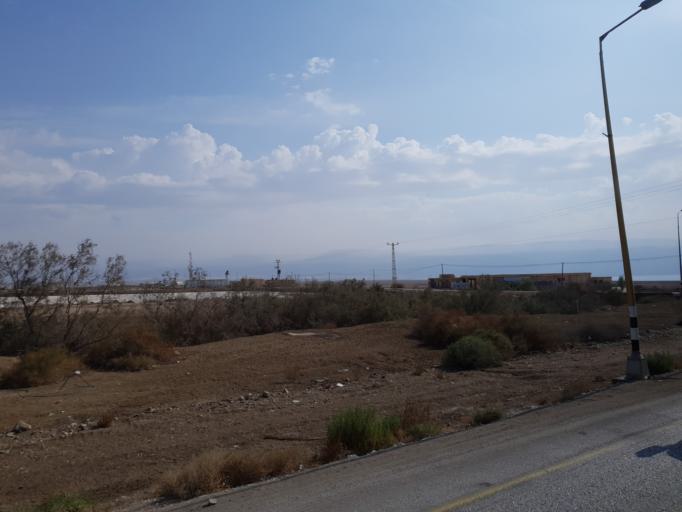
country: PS
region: West Bank
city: Jericho
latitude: 31.7741
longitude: 35.5052
